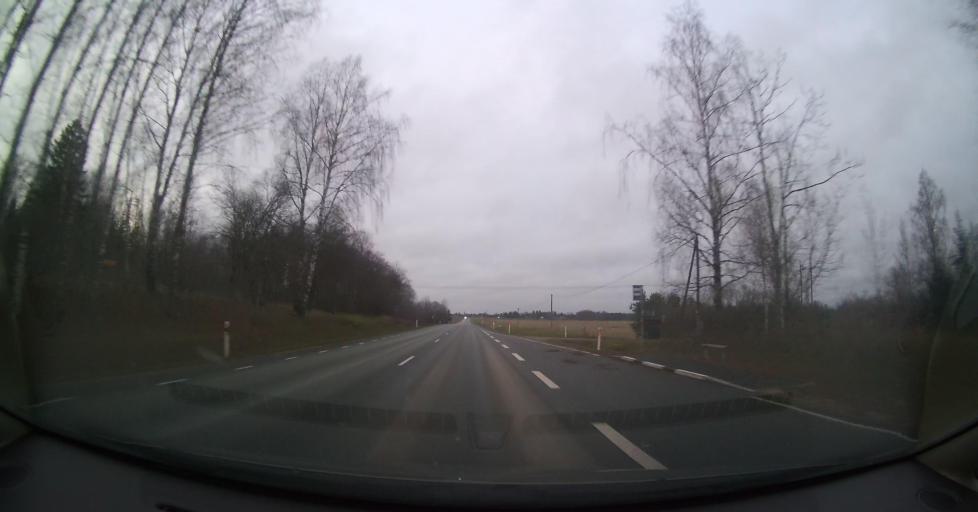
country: EE
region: Laeaene-Virumaa
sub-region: Haljala vald
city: Haljala
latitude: 59.4028
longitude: 26.3035
